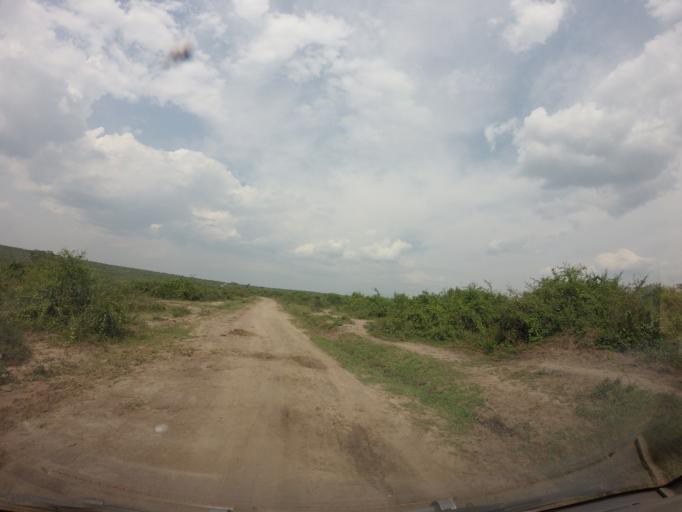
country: UG
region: Western Region
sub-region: Rubirizi District
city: Rubirizi
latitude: -0.2101
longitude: 29.9077
